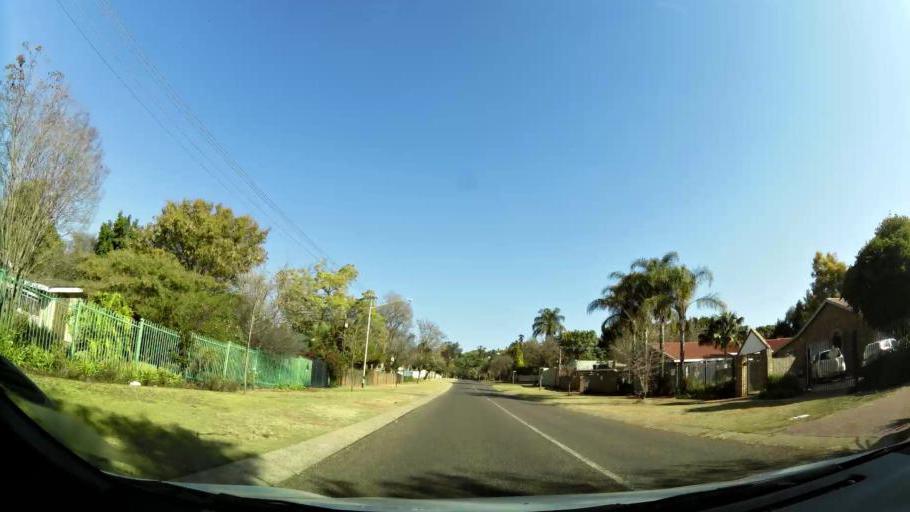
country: ZA
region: Gauteng
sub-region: City of Tshwane Metropolitan Municipality
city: Pretoria
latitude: -25.7853
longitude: 28.2635
